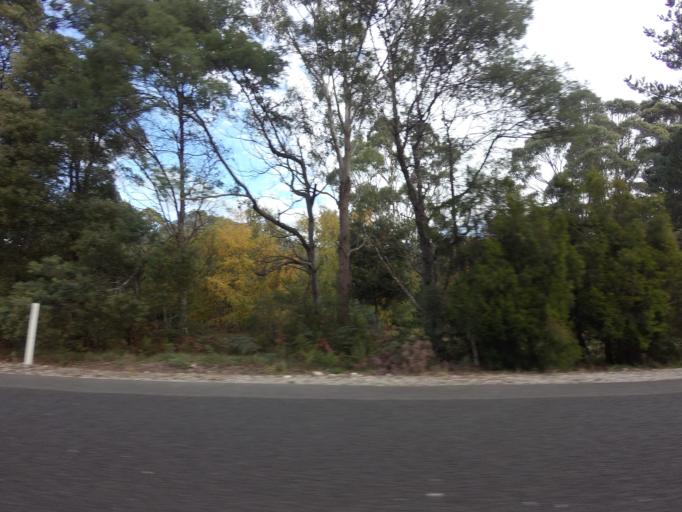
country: AU
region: Tasmania
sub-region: Meander Valley
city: Deloraine
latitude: -41.6195
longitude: 146.6969
